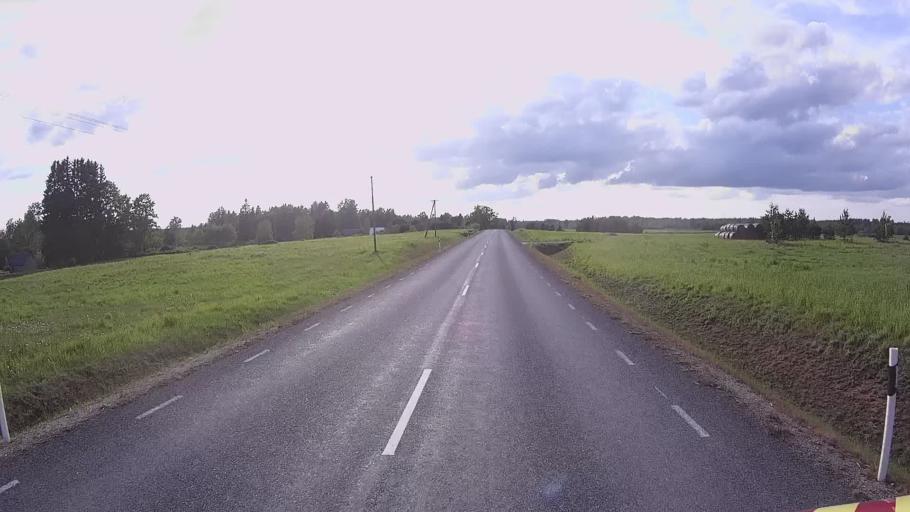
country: EE
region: Jogevamaa
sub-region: Mustvee linn
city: Mustvee
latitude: 59.0448
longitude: 27.0520
